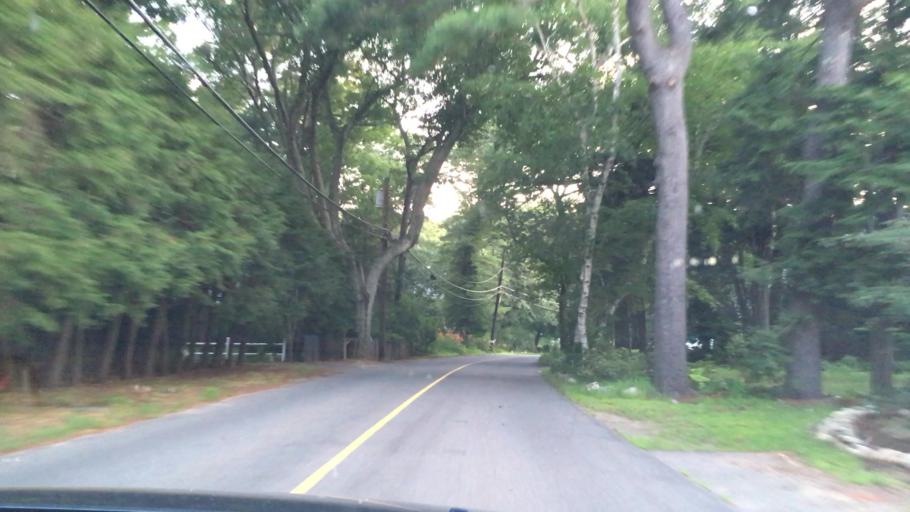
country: US
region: Massachusetts
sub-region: Norfolk County
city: Wellesley
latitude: 42.3272
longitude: -71.2743
